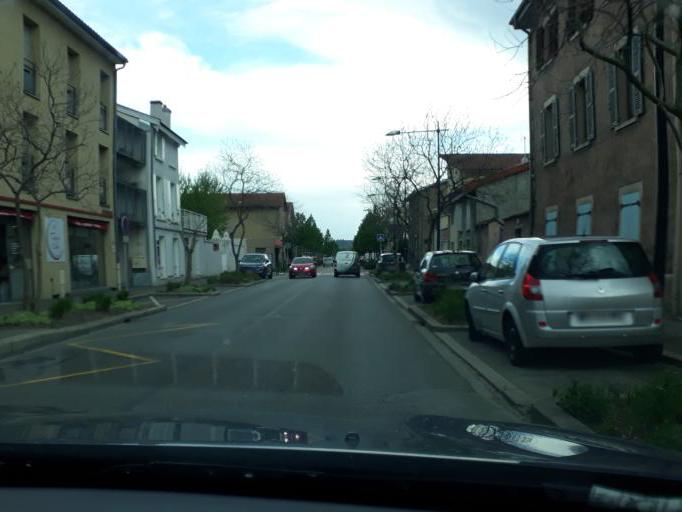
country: FR
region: Rhone-Alpes
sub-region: Departement du Rhone
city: Brignais
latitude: 45.6700
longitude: 4.7531
